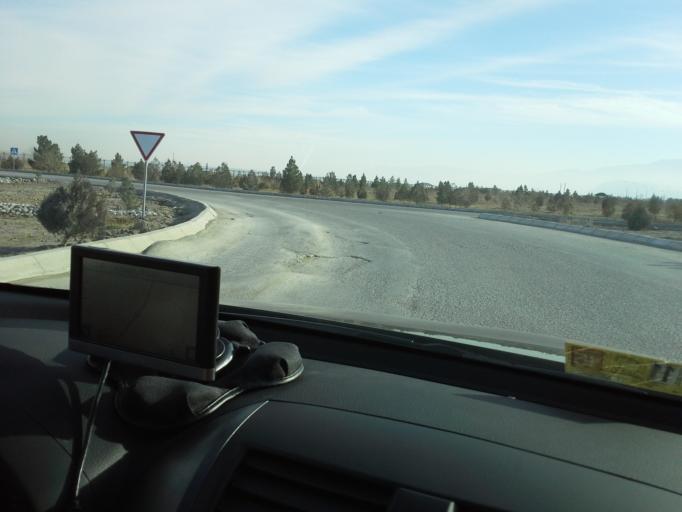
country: TM
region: Ahal
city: Abadan
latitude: 38.0213
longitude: 58.1791
